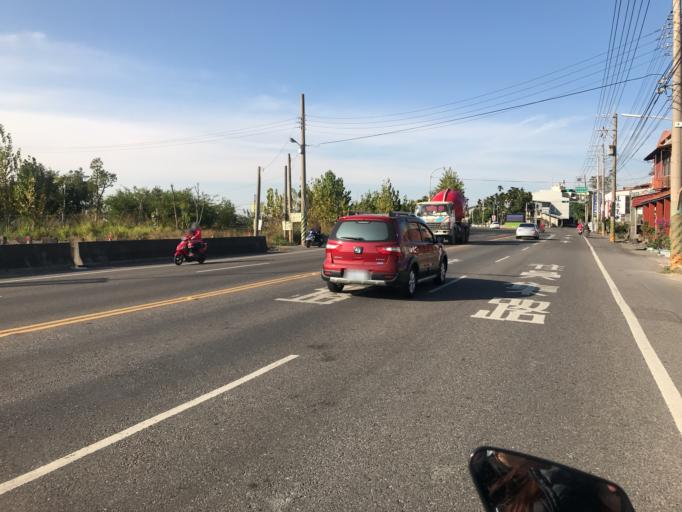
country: TW
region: Taiwan
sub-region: Nantou
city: Nantou
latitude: 23.8850
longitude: 120.5865
